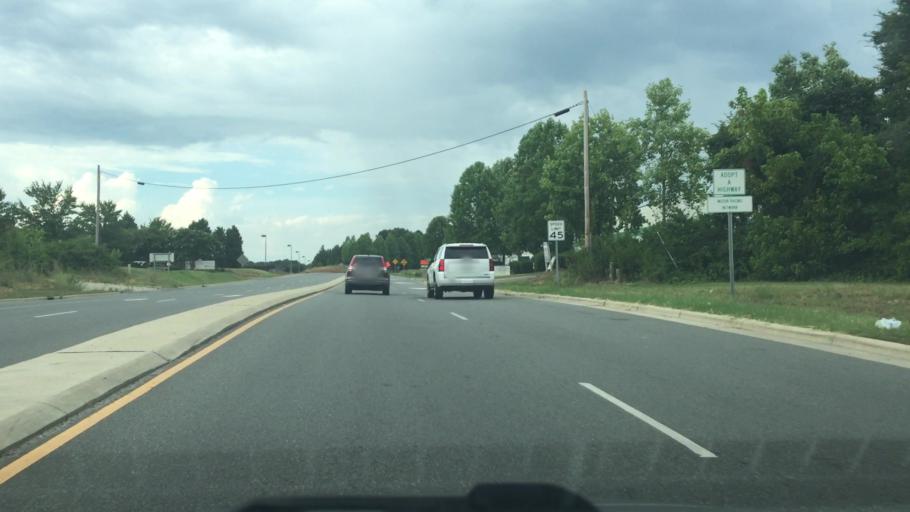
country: US
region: North Carolina
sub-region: Cabarrus County
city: Harrisburg
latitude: 35.4079
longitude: -80.7130
